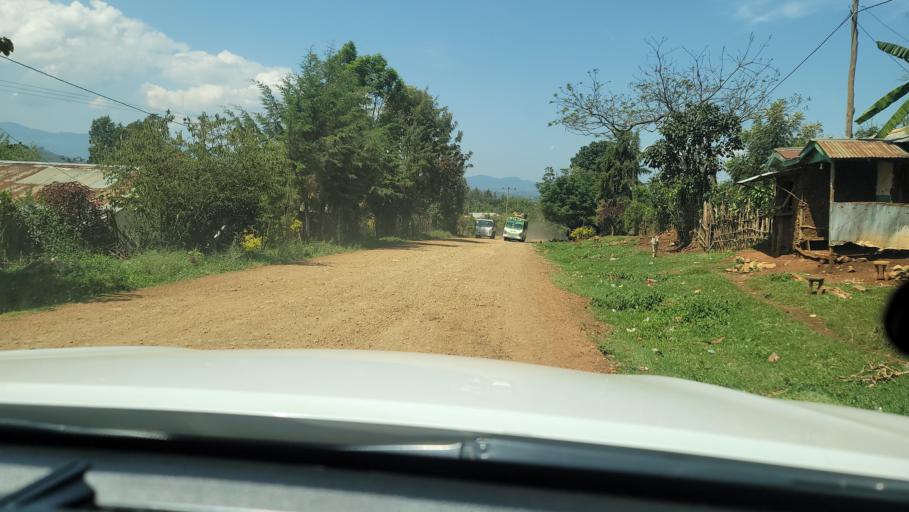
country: ET
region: Oromiya
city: Agaro
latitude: 7.7922
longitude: 36.4416
